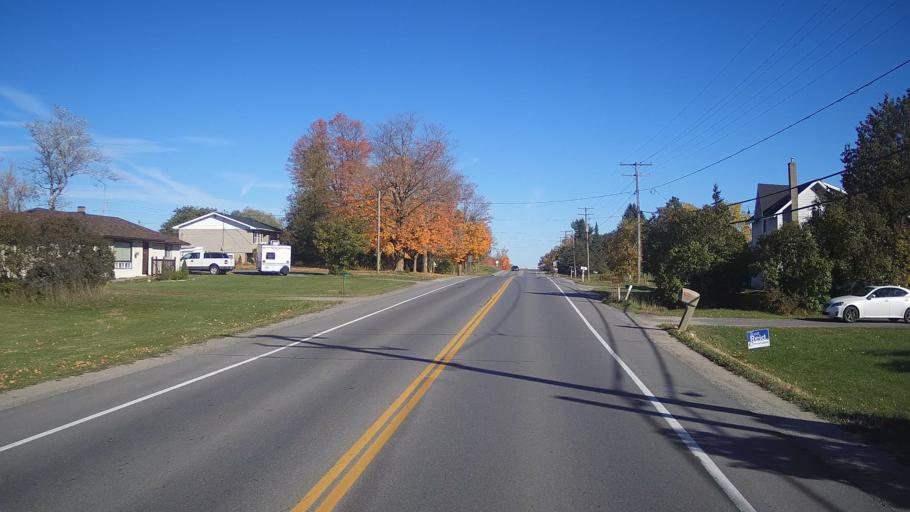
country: CA
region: Ontario
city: Kingston
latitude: 44.4072
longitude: -76.5815
